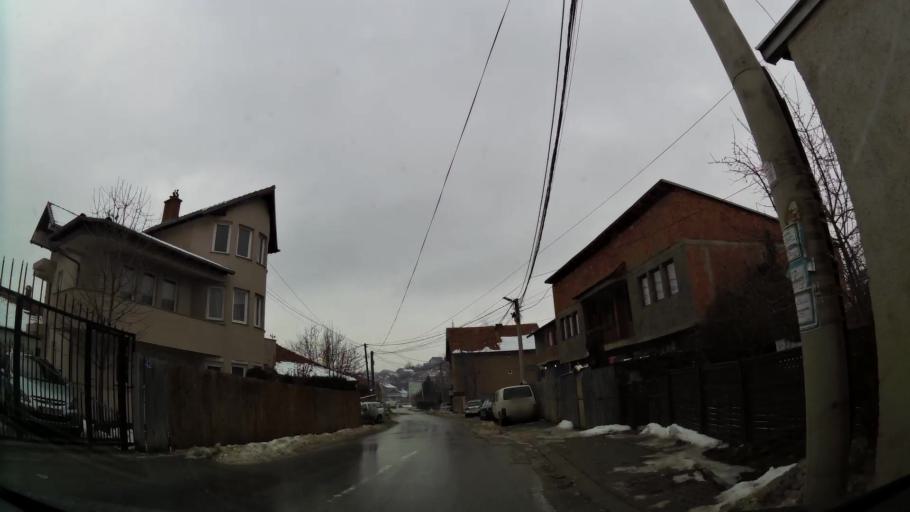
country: XK
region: Pristina
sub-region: Komuna e Prishtines
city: Pristina
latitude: 42.6825
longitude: 21.1784
